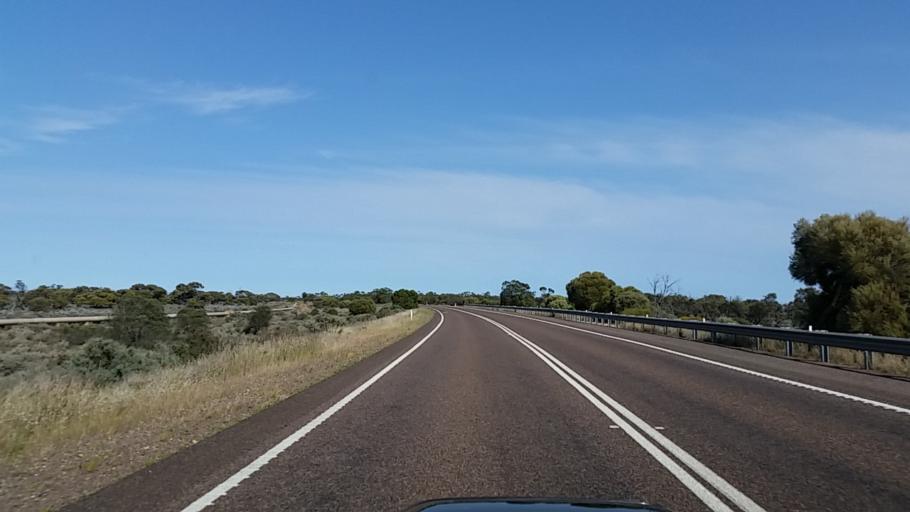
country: AU
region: South Australia
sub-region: Whyalla
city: Whyalla
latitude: -32.8849
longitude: 137.5559
